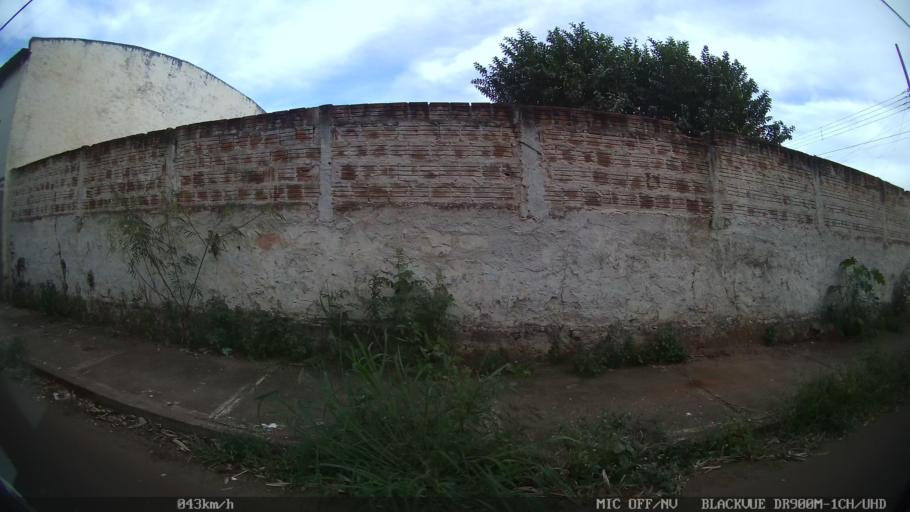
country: BR
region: Sao Paulo
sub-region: Catanduva
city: Catanduva
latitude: -21.1261
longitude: -48.9807
